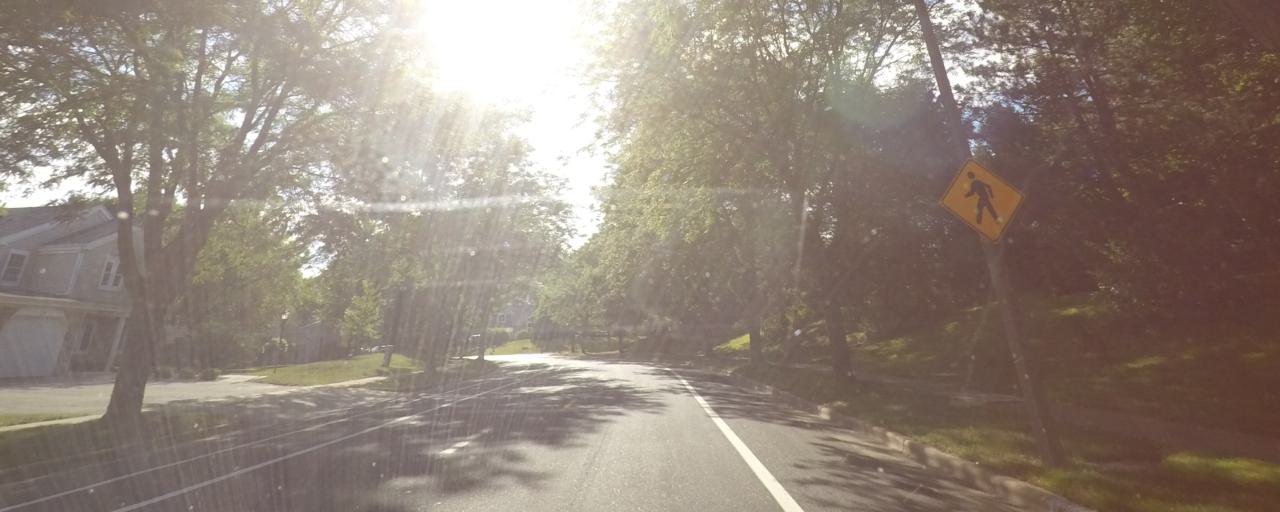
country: US
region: Wisconsin
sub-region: Dane County
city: Middleton
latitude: 43.0641
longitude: -89.5183
